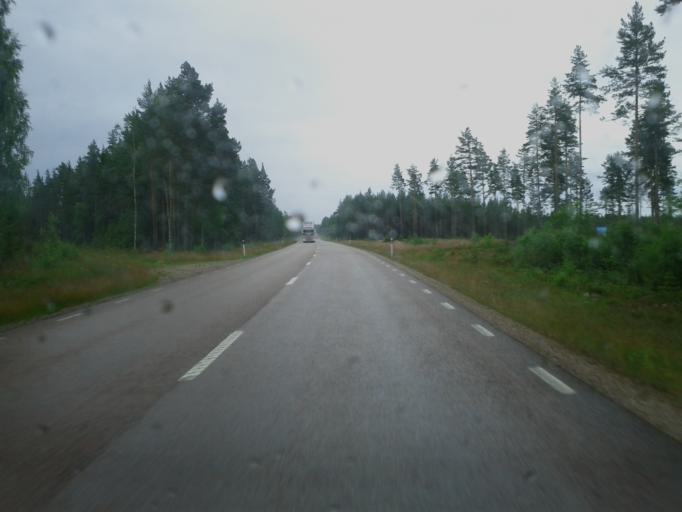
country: SE
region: Dalarna
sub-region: Mora Kommun
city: Mora
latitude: 60.9726
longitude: 14.6980
